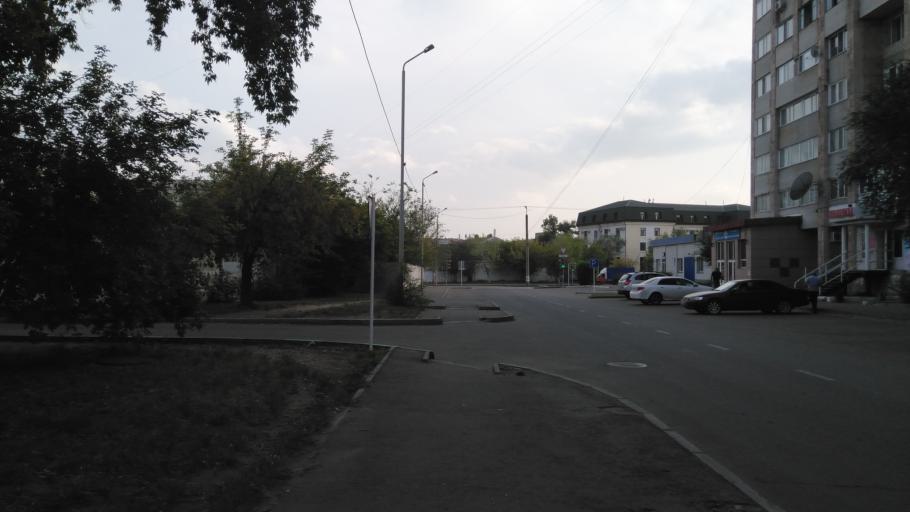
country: KZ
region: Pavlodar
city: Pavlodar
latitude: 52.2998
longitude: 76.9468
